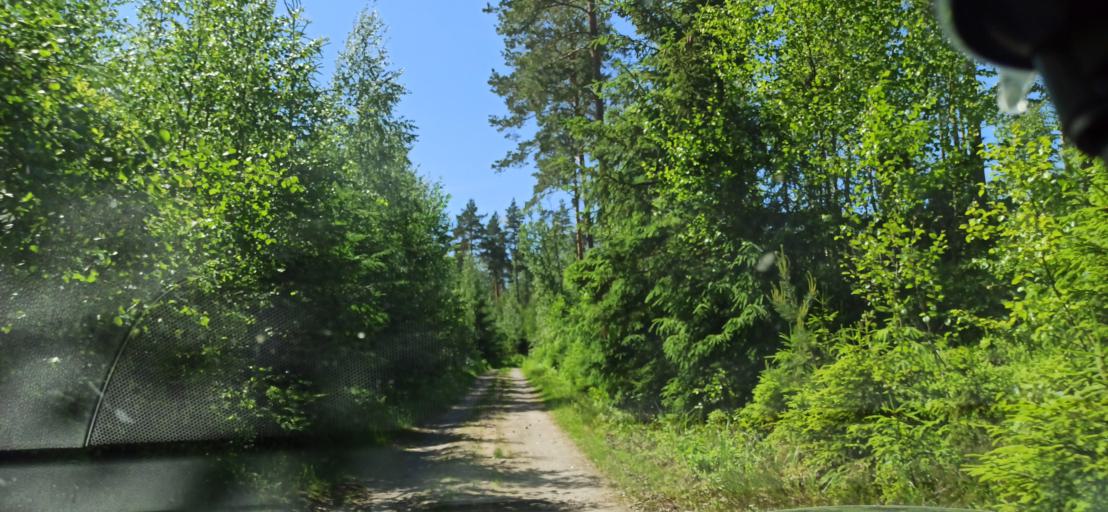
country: FI
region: Varsinais-Suomi
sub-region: Turku
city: Sauvo
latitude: 60.3799
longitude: 22.6223
